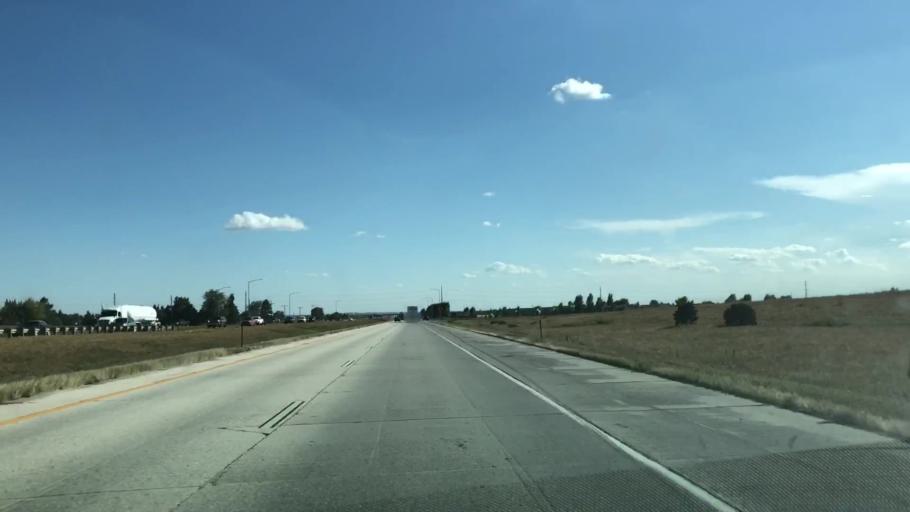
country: US
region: Colorado
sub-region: Larimer County
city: Fort Collins
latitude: 40.6095
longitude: -105.0025
